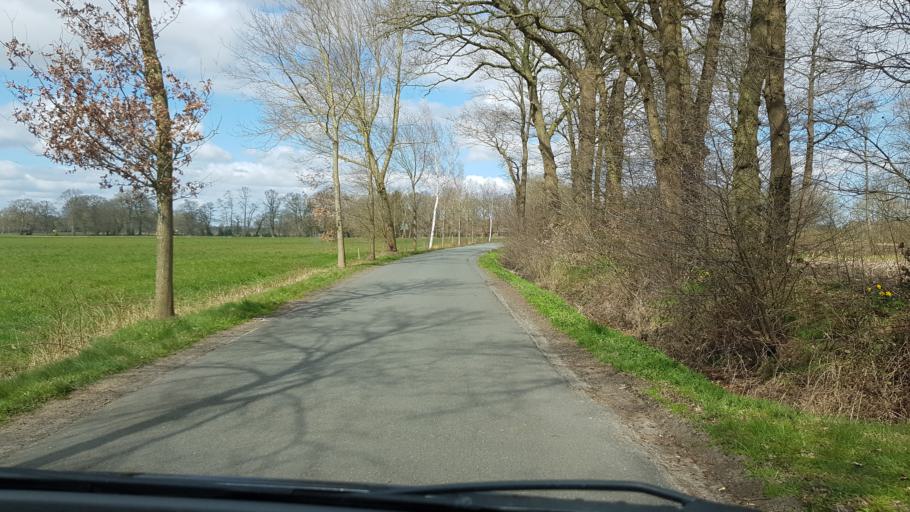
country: DE
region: Lower Saxony
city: Edewecht
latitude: 53.1033
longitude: 7.9443
